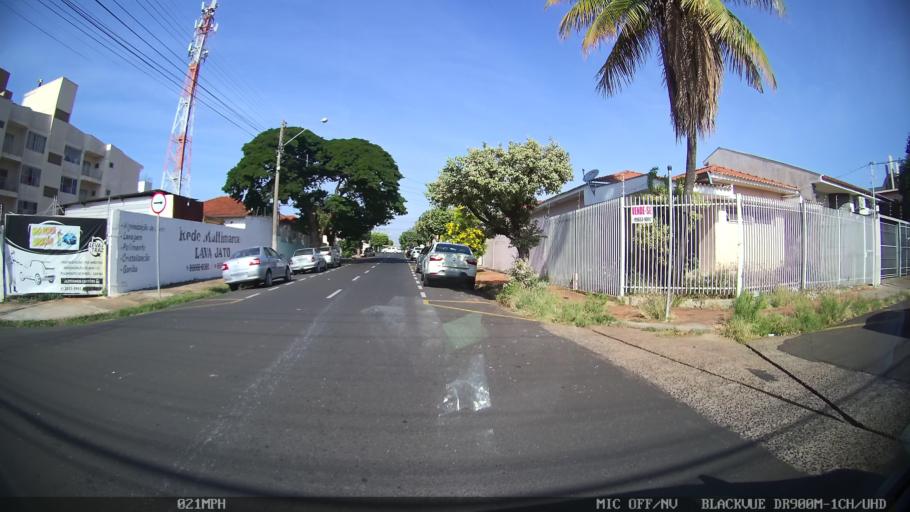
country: BR
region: Sao Paulo
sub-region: Sao Jose Do Rio Preto
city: Sao Jose do Rio Preto
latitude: -20.8020
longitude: -49.3911
